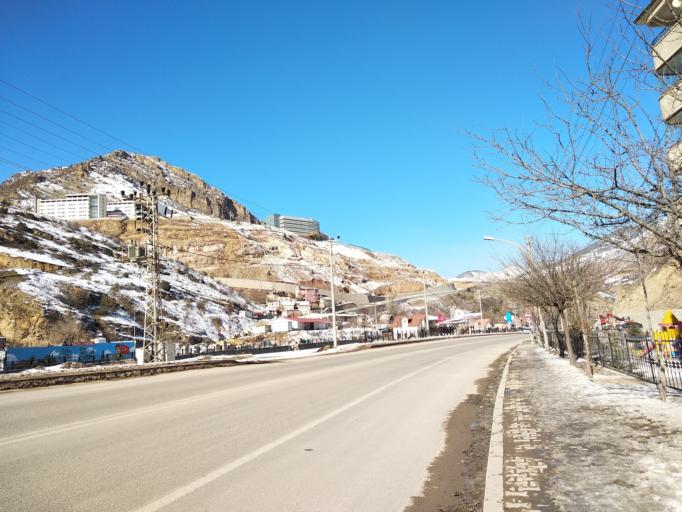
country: TR
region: Gumushane
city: Gumushkhane
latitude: 40.4384
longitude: 39.5048
